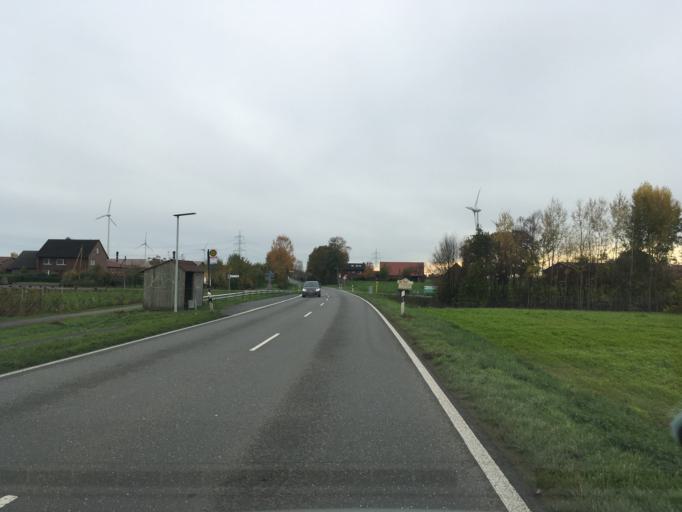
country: DE
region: North Rhine-Westphalia
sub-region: Regierungsbezirk Munster
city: Heiden
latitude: 51.8140
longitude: 6.9467
